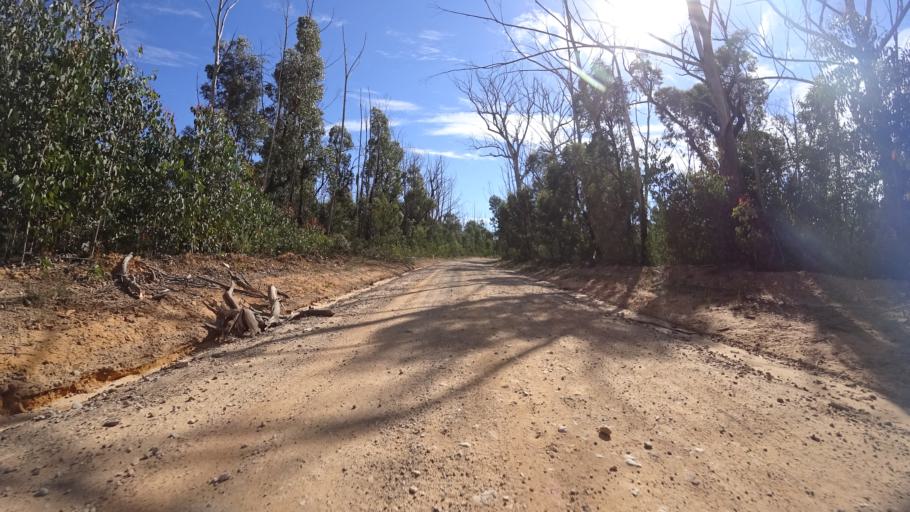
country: AU
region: New South Wales
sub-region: Lithgow
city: Lithgow
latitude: -33.4354
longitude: 150.1847
